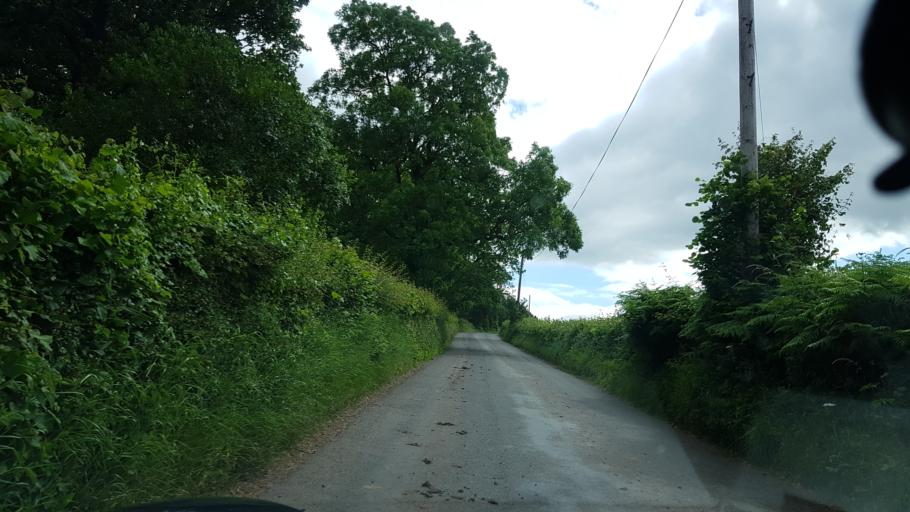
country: GB
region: England
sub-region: Herefordshire
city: Llancillo
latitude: 51.8866
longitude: -2.9508
